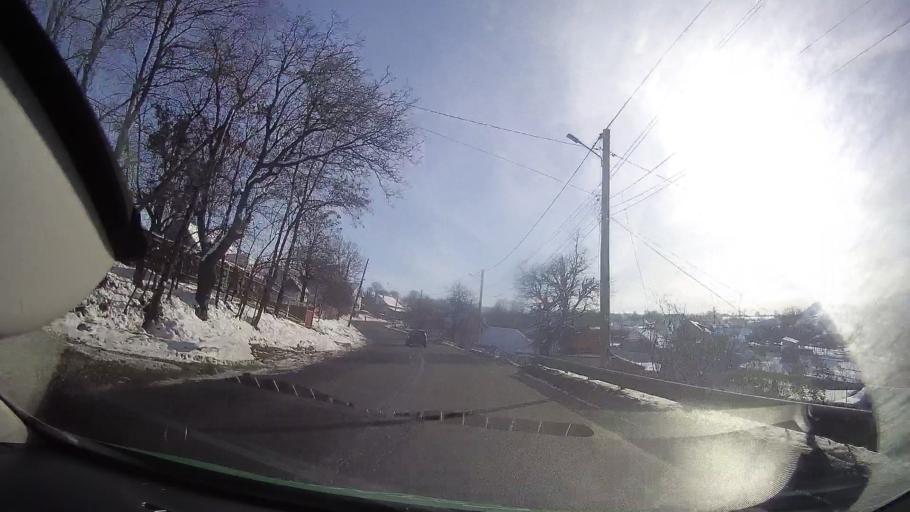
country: RO
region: Neamt
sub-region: Comuna Baltatesti
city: Baltatesti
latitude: 47.1152
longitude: 26.3128
